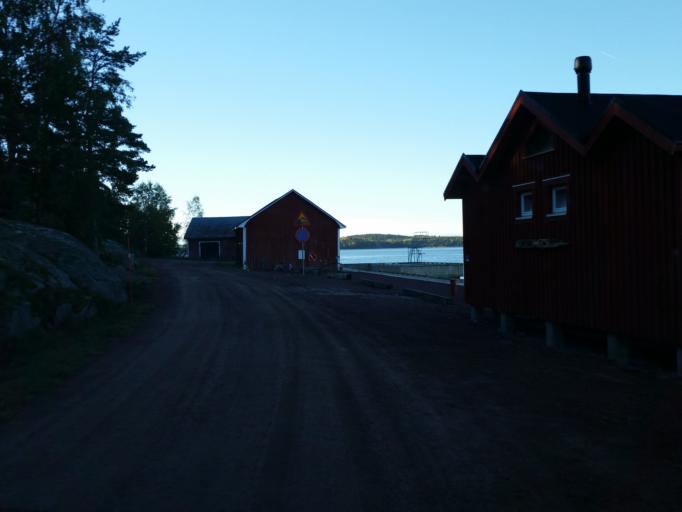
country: AX
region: Alands skaergard
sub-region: Vardoe
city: Vardoe
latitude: 60.2425
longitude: 20.3278
